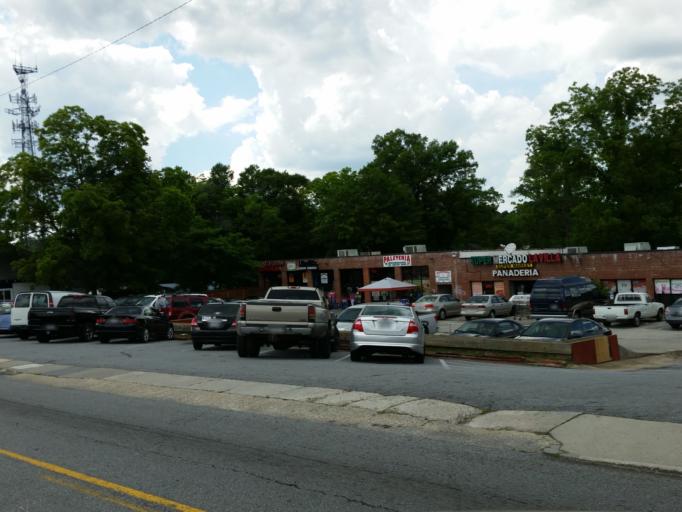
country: US
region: Georgia
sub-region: Cobb County
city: Marietta
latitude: 33.9506
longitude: -84.5305
